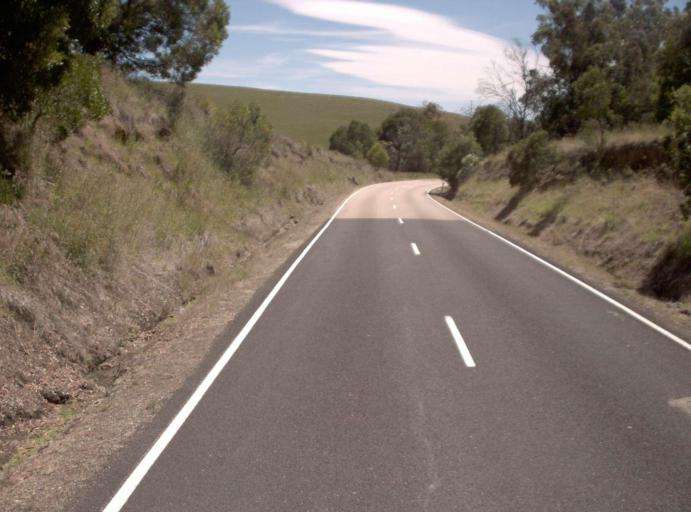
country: AU
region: Victoria
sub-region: East Gippsland
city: Lakes Entrance
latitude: -37.2529
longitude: 148.2489
